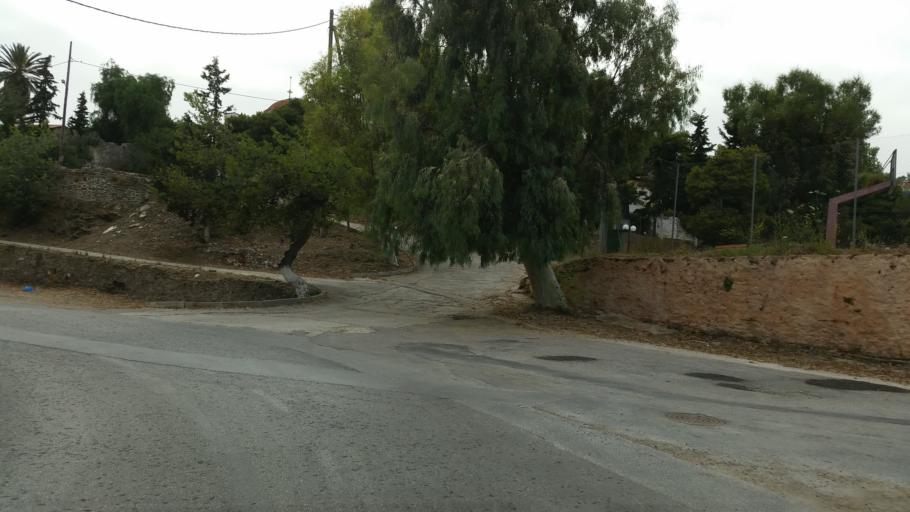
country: GR
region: Attica
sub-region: Nomarchia Anatolikis Attikis
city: Lavrio
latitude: 37.7259
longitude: 24.0153
